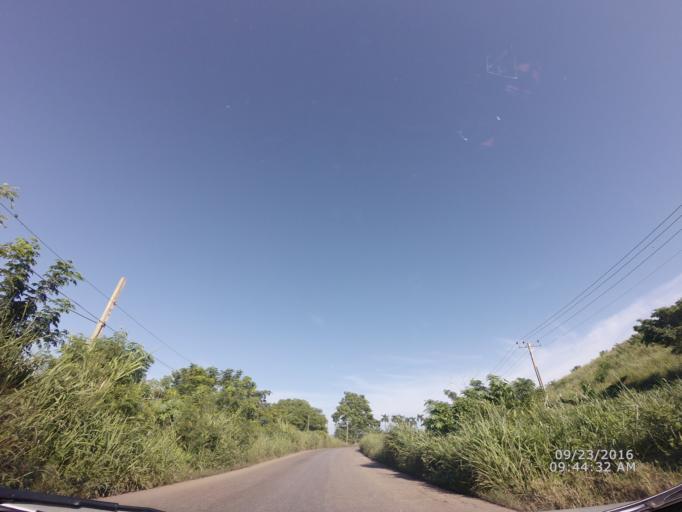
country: CU
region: Mayabeque
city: Bejucal
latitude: 22.9459
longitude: -82.4098
